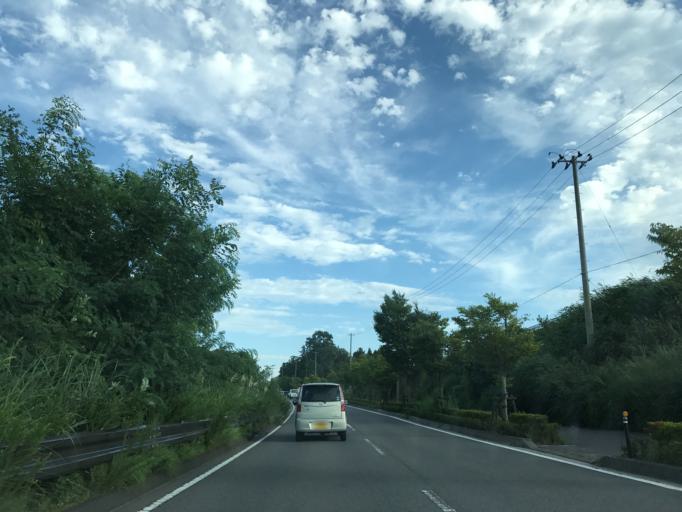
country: JP
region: Fukushima
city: Koriyama
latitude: 37.3561
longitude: 140.3261
